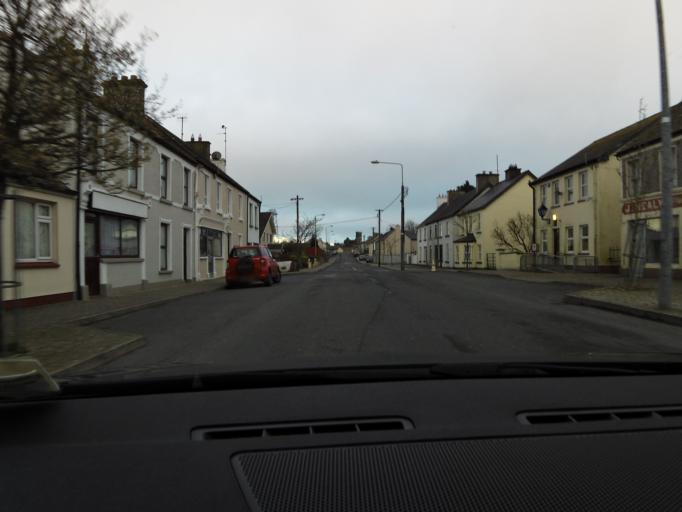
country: IE
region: Connaught
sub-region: Sligo
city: Ballymote
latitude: 53.9932
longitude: -8.5159
